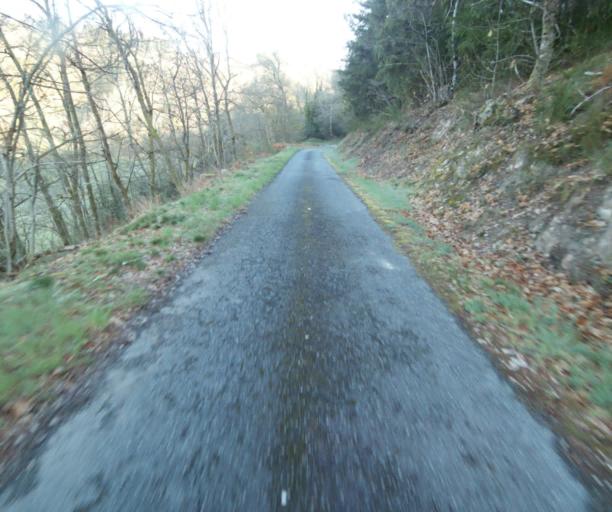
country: FR
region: Limousin
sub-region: Departement de la Correze
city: Correze
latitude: 45.3746
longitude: 1.8455
